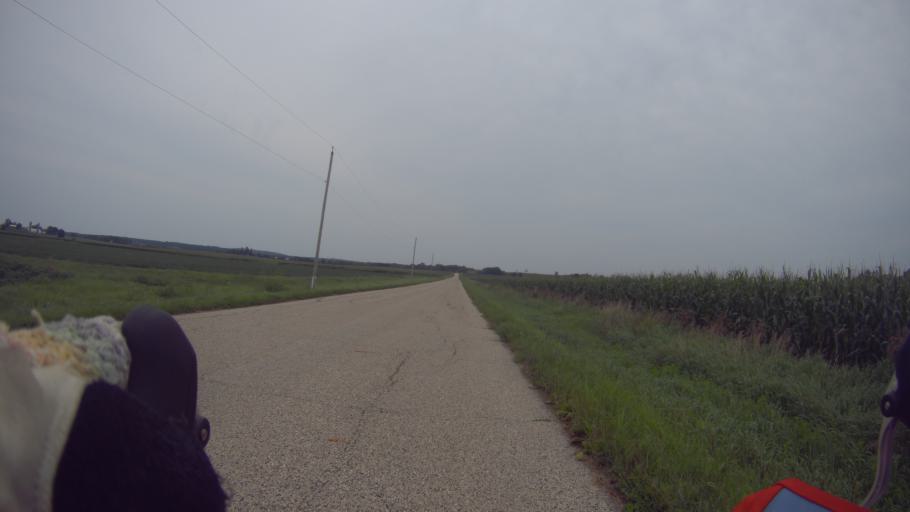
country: US
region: Wisconsin
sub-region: Dane County
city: Verona
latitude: 42.9296
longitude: -89.5560
